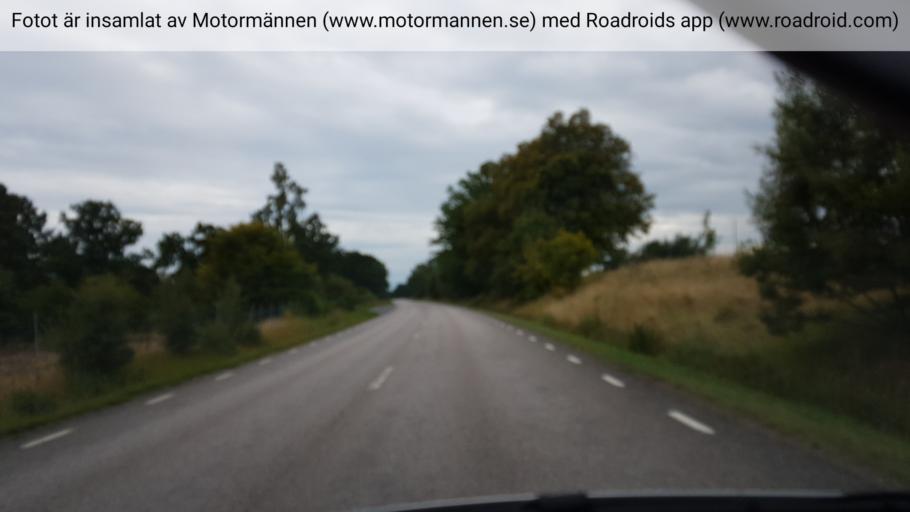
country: SE
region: Vaestra Goetaland
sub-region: Hjo Kommun
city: Hjo
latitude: 58.3398
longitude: 14.3380
